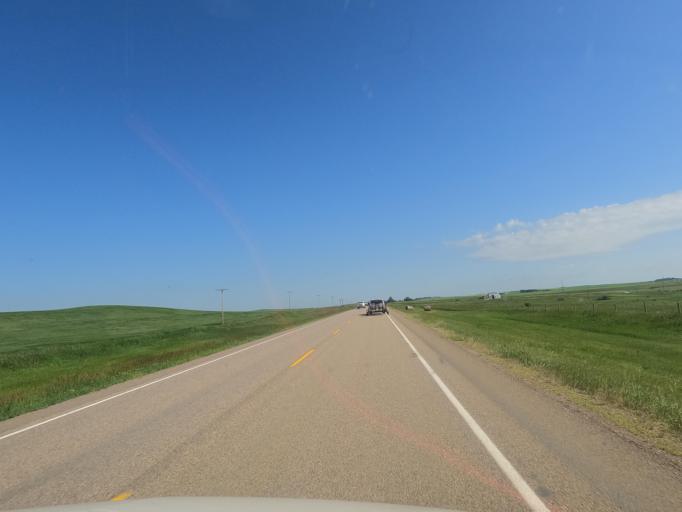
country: CA
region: Saskatchewan
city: Shaunavon
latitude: 49.9341
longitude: -108.4849
